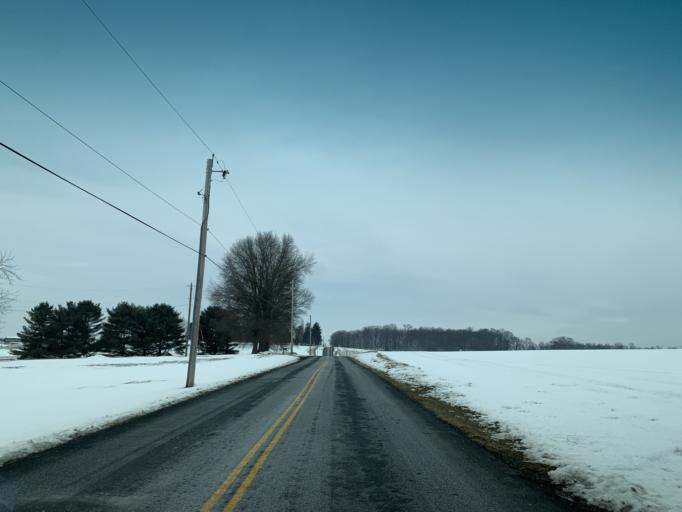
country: US
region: Pennsylvania
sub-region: York County
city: Susquehanna Trails
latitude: 39.7100
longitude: -76.4195
